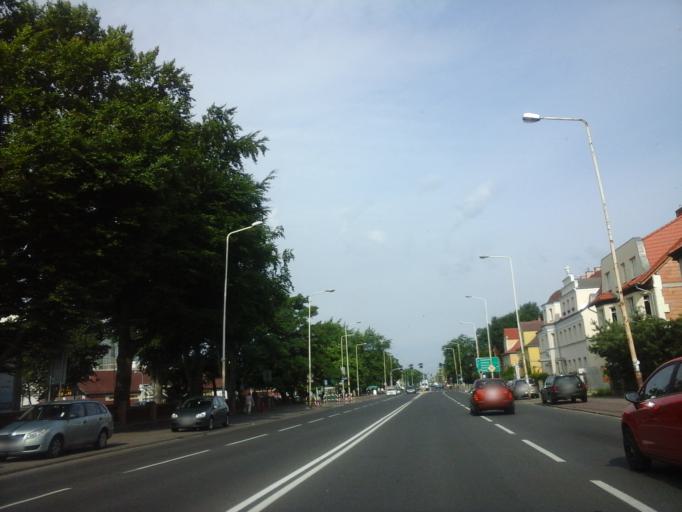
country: PL
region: West Pomeranian Voivodeship
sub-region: Powiat stargardzki
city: Stargard Szczecinski
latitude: 53.3395
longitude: 15.0223
